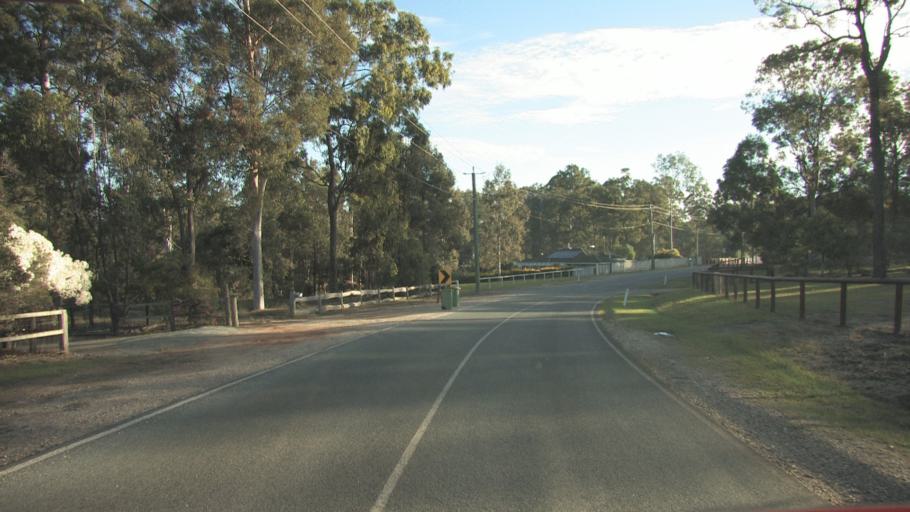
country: AU
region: Queensland
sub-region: Logan
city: Waterford West
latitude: -27.7328
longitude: 153.1402
